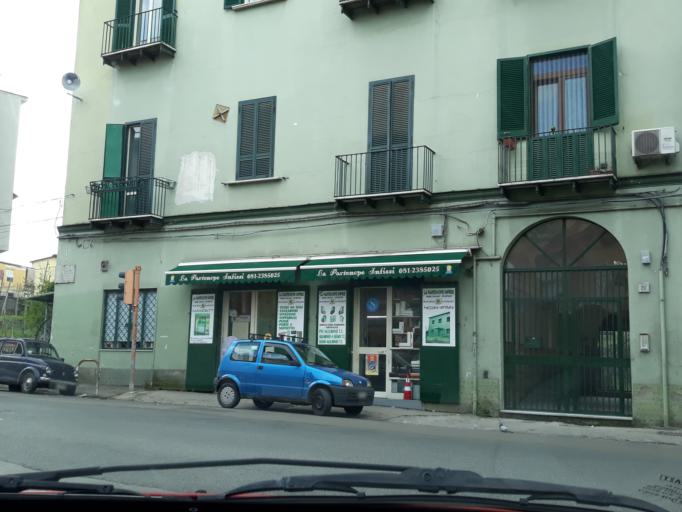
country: IT
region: Campania
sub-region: Provincia di Napoli
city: Mugnano di Napoli
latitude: 40.8858
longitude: 14.2288
